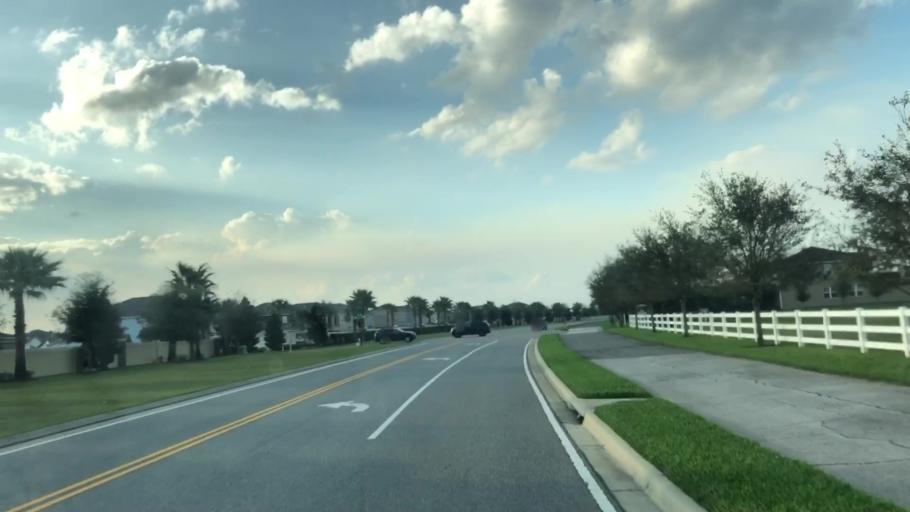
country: US
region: Florida
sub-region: Orange County
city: Lake Butler
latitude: 28.4488
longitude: -81.6211
